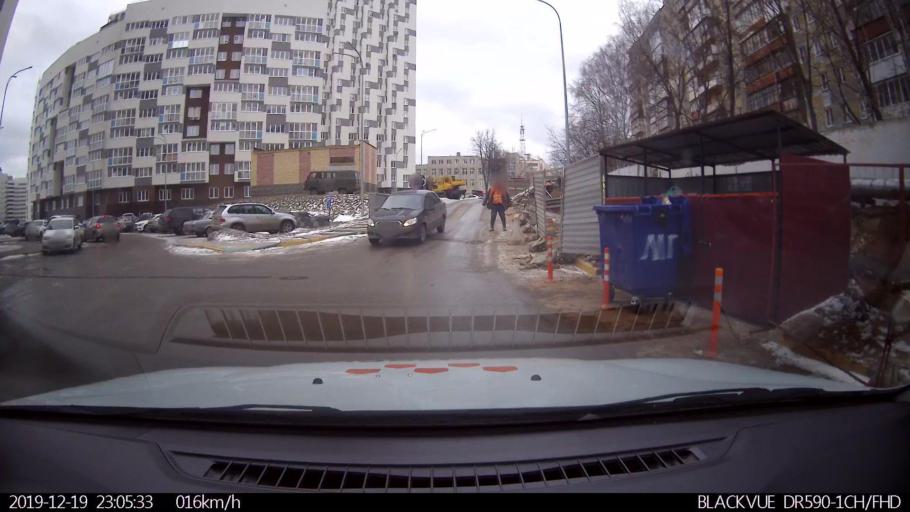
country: RU
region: Nizjnij Novgorod
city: Nizhniy Novgorod
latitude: 56.3007
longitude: 43.9784
